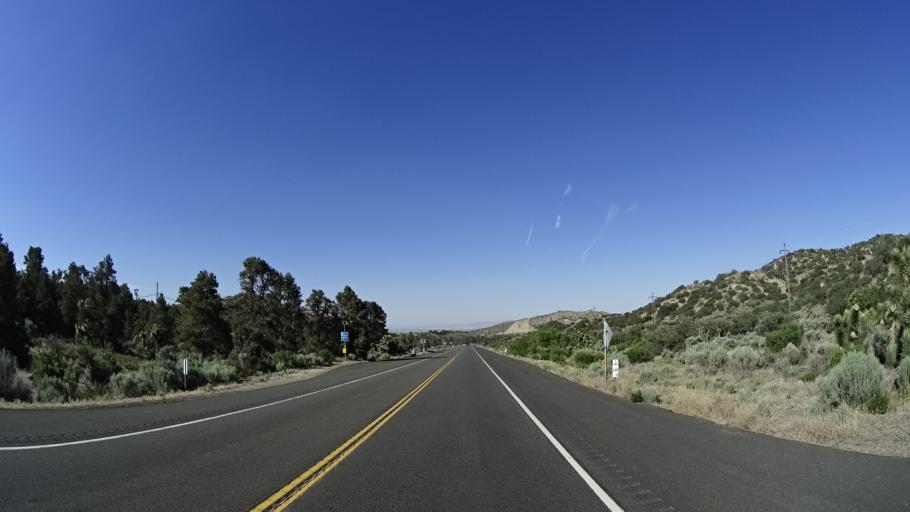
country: US
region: California
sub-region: San Bernardino County
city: Wrightwood
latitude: 34.3808
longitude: -117.5964
